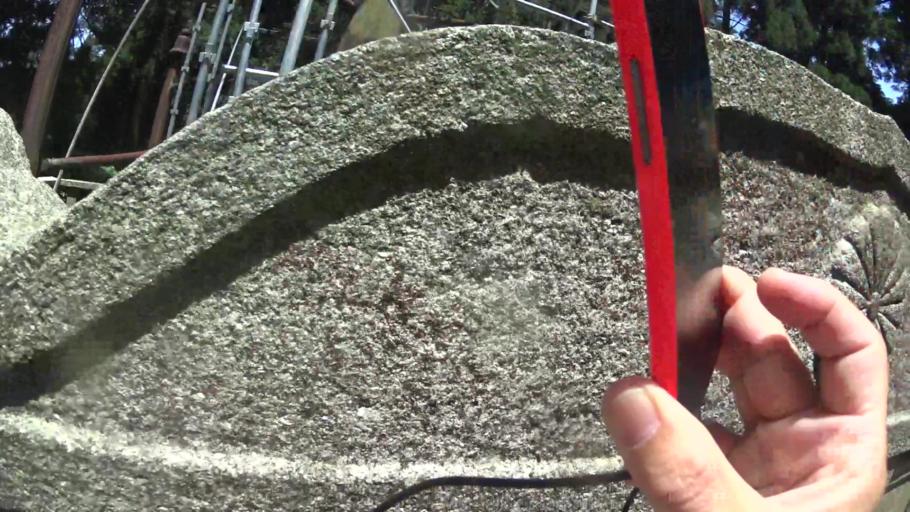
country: JP
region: Shiga Prefecture
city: Otsu-shi
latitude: 35.0755
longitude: 135.8341
